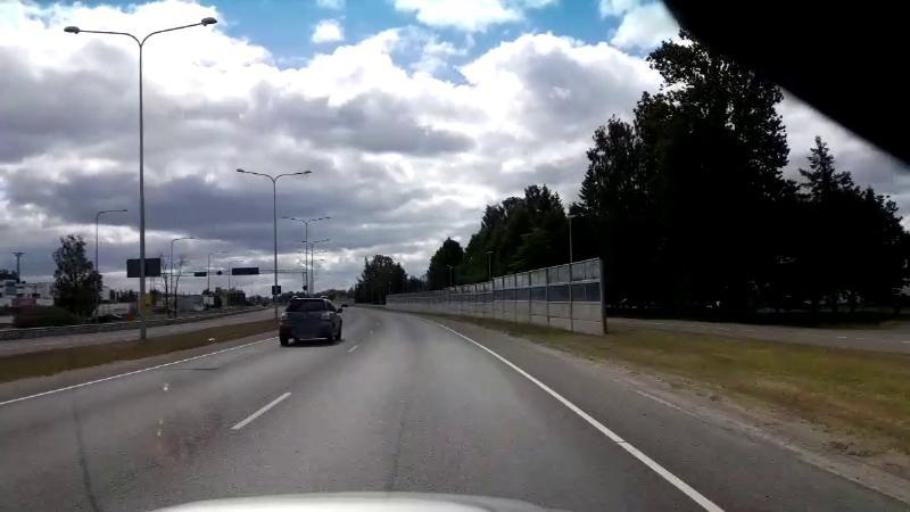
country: EE
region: Paernumaa
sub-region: Paernu linn
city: Parnu
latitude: 58.4037
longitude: 24.5030
